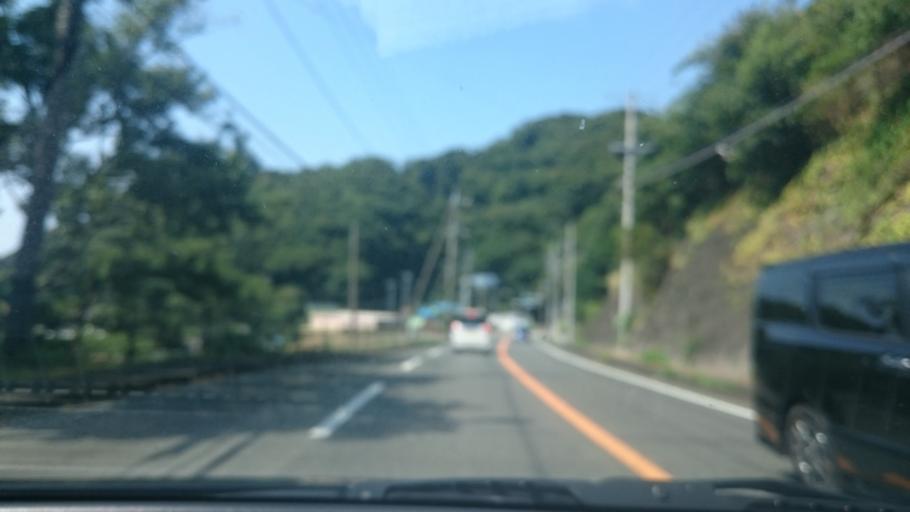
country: JP
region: Shizuoka
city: Heda
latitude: 34.8215
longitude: 138.7702
